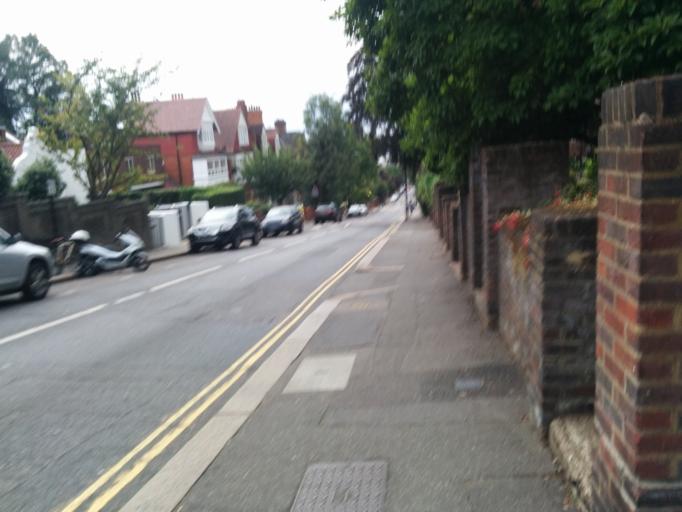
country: GB
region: England
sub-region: Greater London
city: Belsize Park
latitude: 51.5526
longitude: -0.1789
